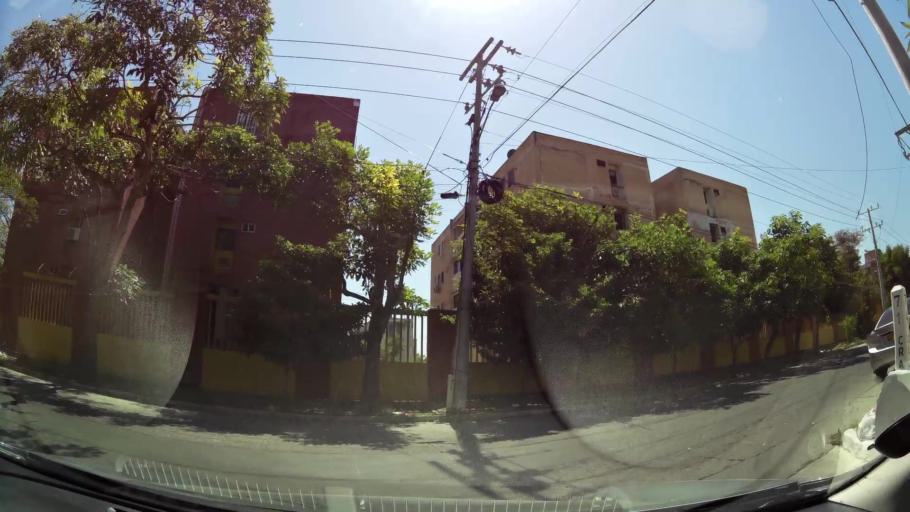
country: CO
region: Atlantico
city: Barranquilla
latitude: 11.0091
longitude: -74.7933
